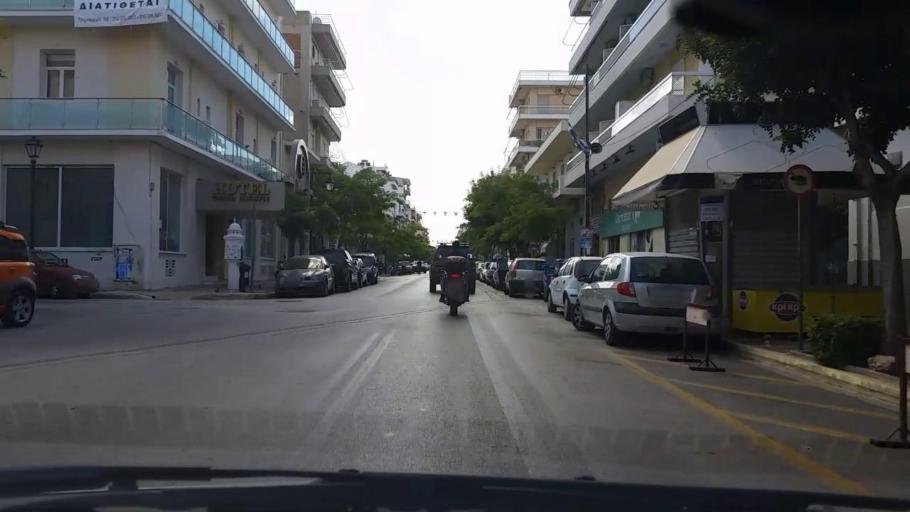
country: GR
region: Peloponnese
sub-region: Nomos Korinthias
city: Loutraki
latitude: 37.9778
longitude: 22.9773
